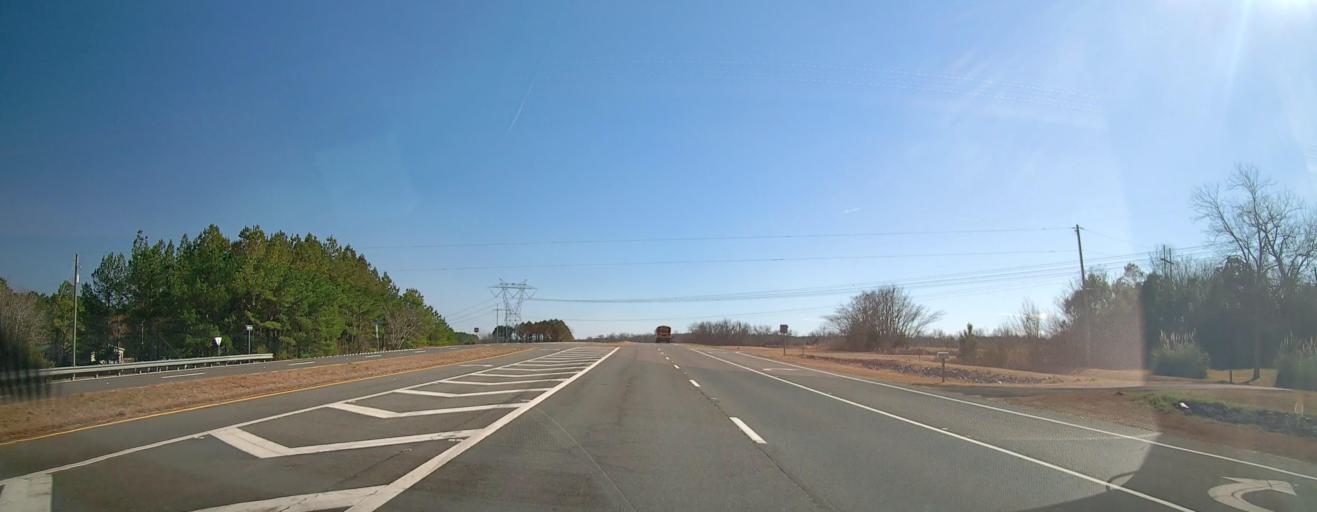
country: US
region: Georgia
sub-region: Sumter County
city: Americus
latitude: 32.1503
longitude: -84.2697
